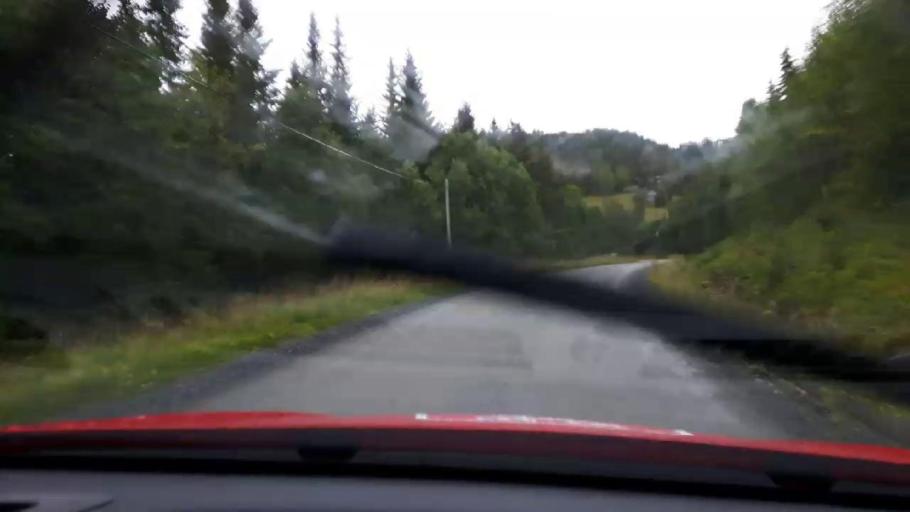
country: SE
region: Jaemtland
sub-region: Are Kommun
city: Are
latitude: 63.4581
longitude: 12.8164
